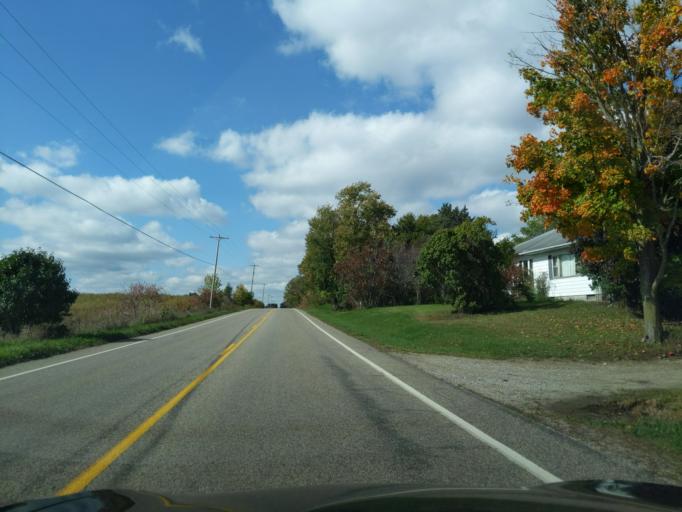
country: US
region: Michigan
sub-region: Eaton County
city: Potterville
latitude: 42.5676
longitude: -84.7616
